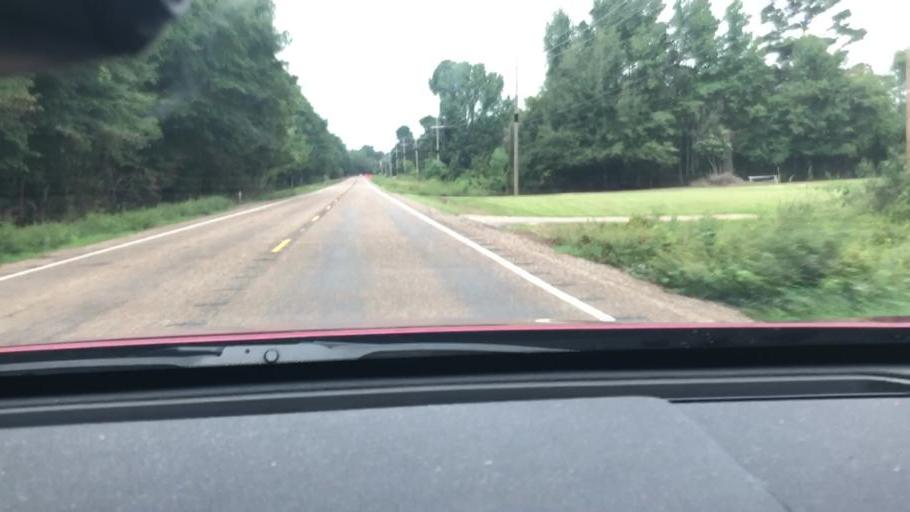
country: US
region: Texas
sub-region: Bowie County
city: Wake Village
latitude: 33.3792
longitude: -94.1027
